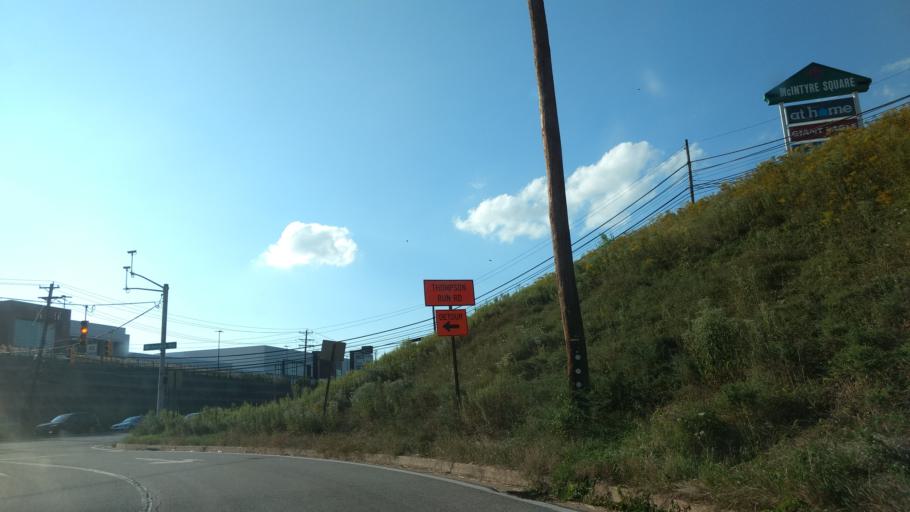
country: US
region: Pennsylvania
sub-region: Allegheny County
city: West View
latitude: 40.5505
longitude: -80.0188
